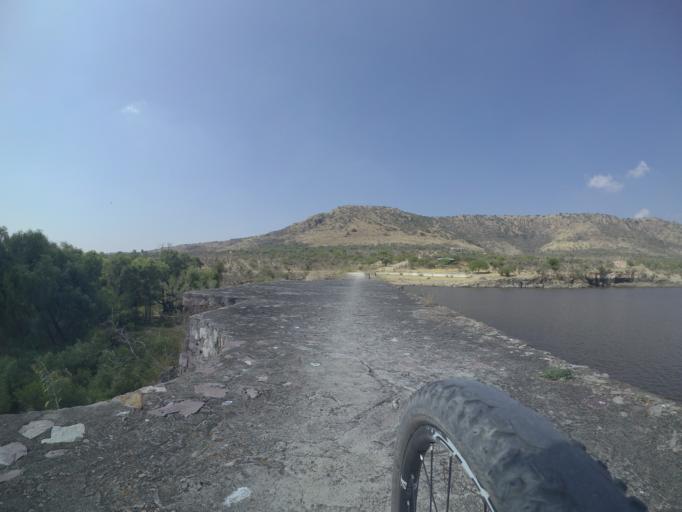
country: MX
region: Aguascalientes
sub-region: Jesus Maria
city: Paseos de las Haciendas [Fraccionamiento]
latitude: 22.0060
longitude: -102.3717
